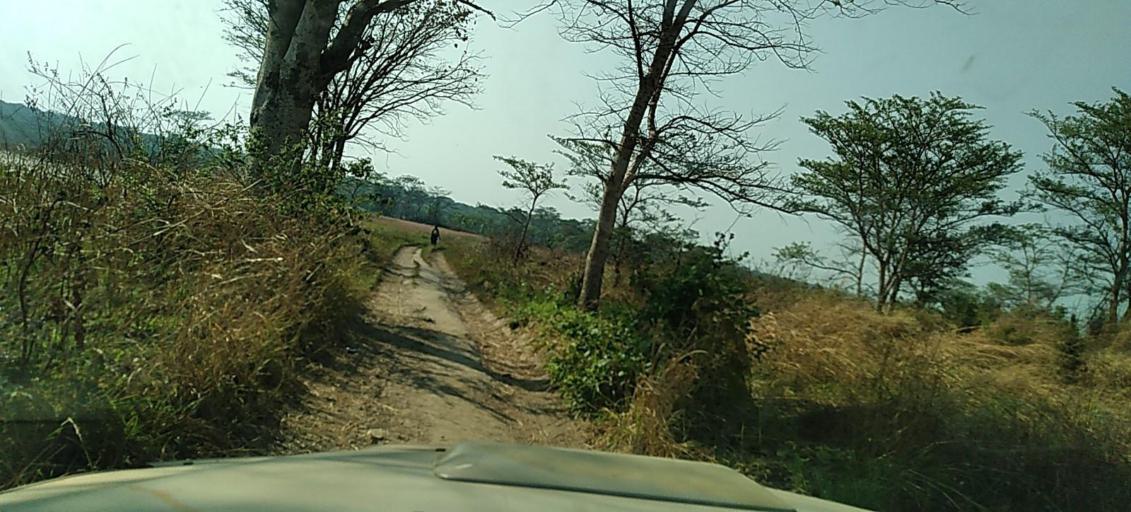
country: ZM
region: North-Western
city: Kasempa
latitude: -13.1872
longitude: 25.9675
